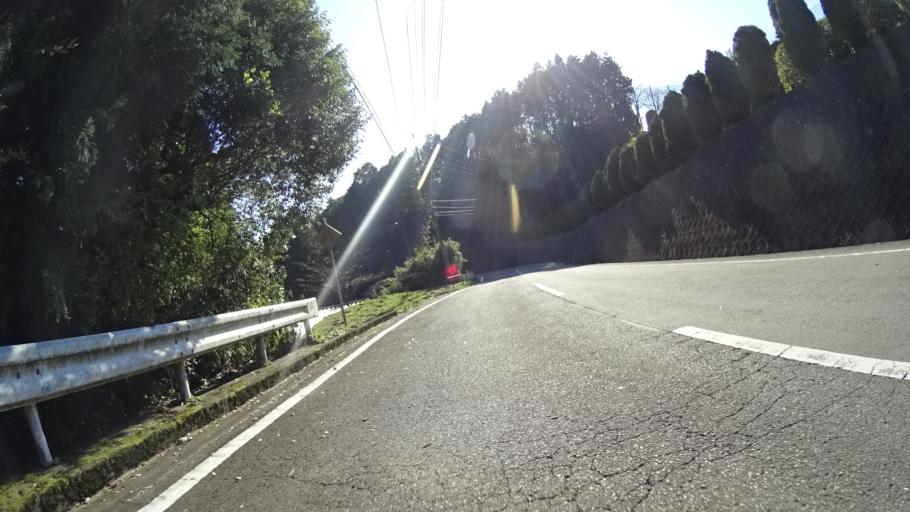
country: JP
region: Yamanashi
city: Uenohara
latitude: 35.6597
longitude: 139.1197
